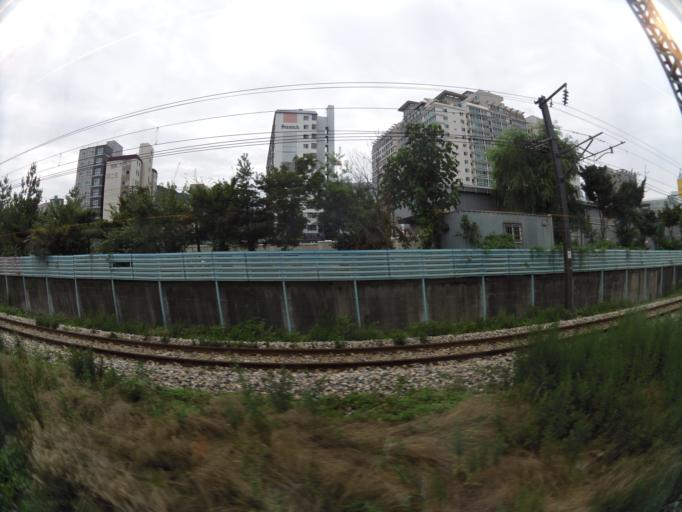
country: KR
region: Gyeonggi-do
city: Anyang-si
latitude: 37.3911
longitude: 126.9330
